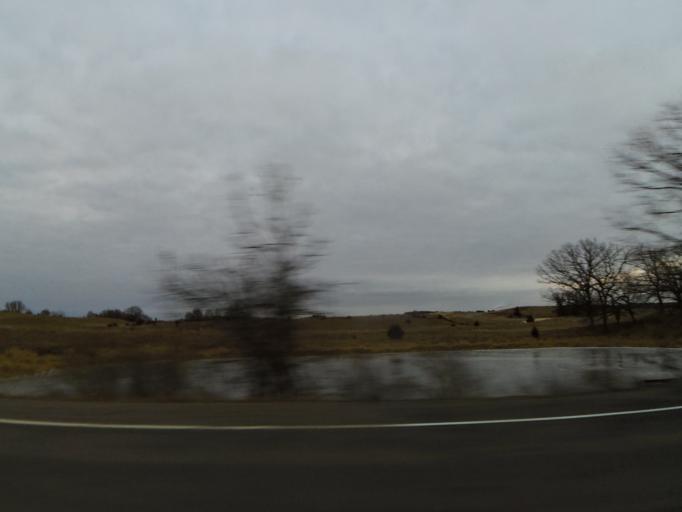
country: US
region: Minnesota
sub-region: Washington County
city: Grant
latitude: 45.0538
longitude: -92.8836
